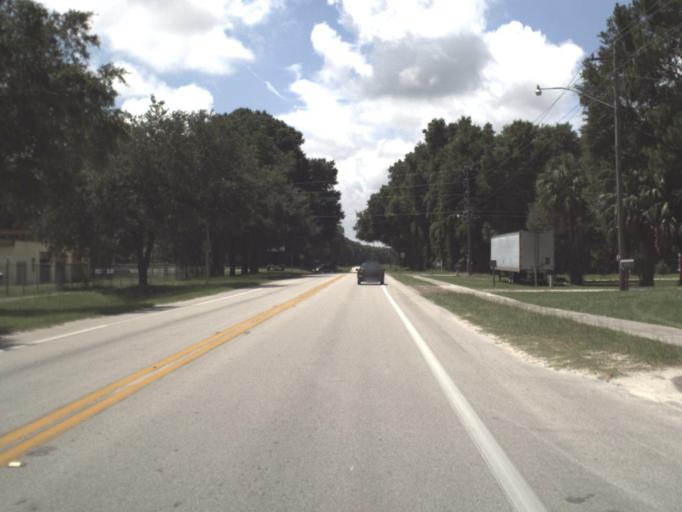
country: US
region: Florida
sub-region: Gilchrist County
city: Trenton
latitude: 29.7499
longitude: -82.8603
